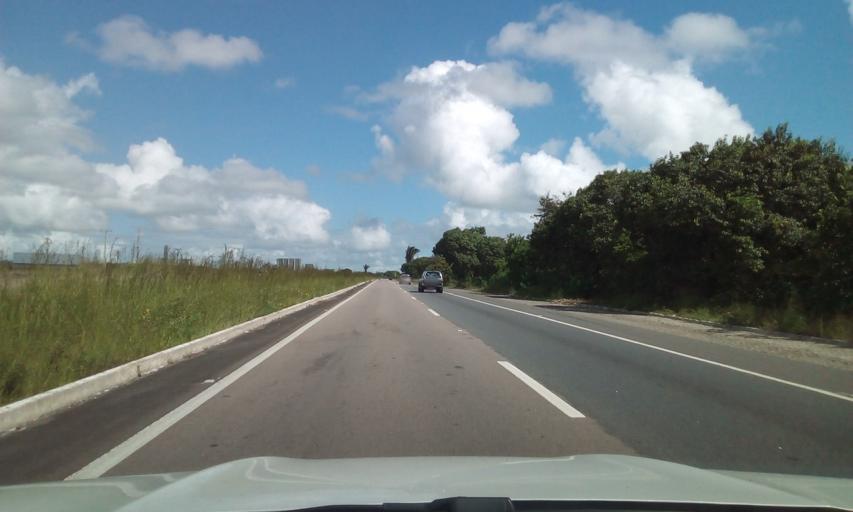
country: BR
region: Paraiba
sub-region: Conde
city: Conde
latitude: -7.2775
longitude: -34.9387
